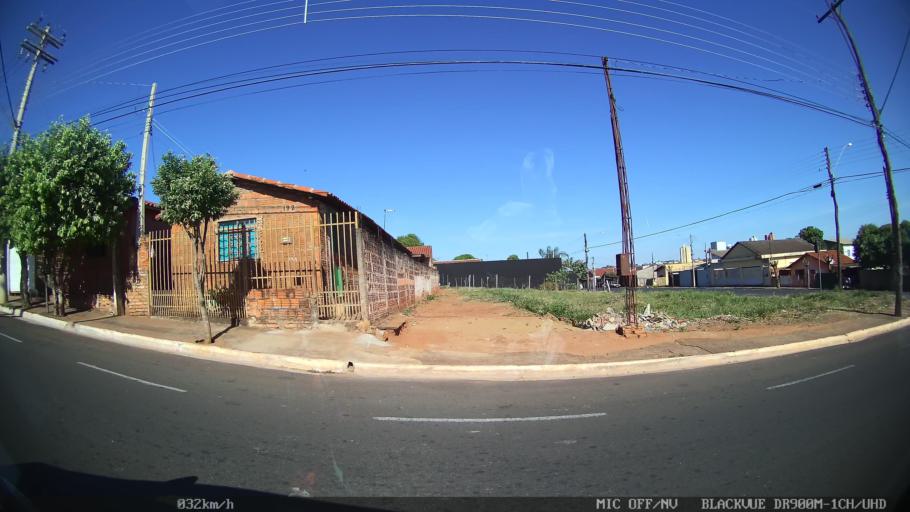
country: BR
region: Sao Paulo
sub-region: Olimpia
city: Olimpia
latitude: -20.7271
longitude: -48.9132
